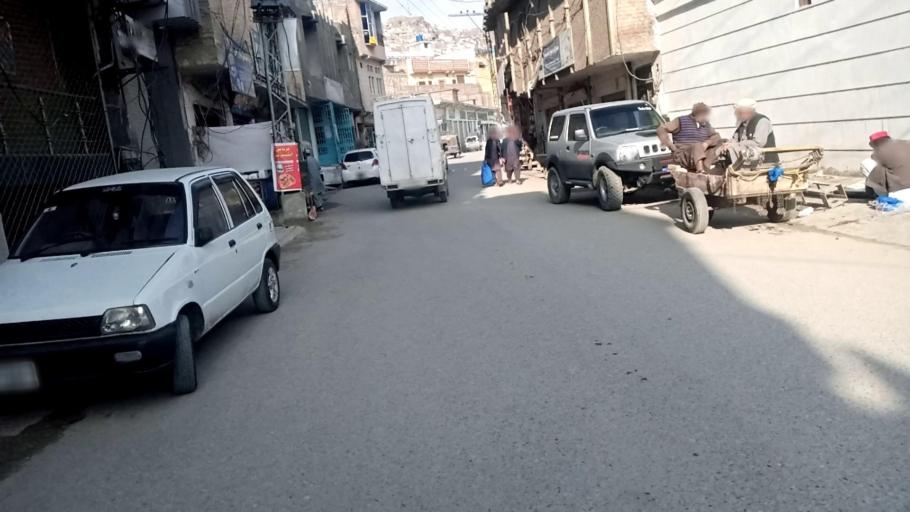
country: PK
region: Khyber Pakhtunkhwa
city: Mingora
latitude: 34.7749
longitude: 72.3632
